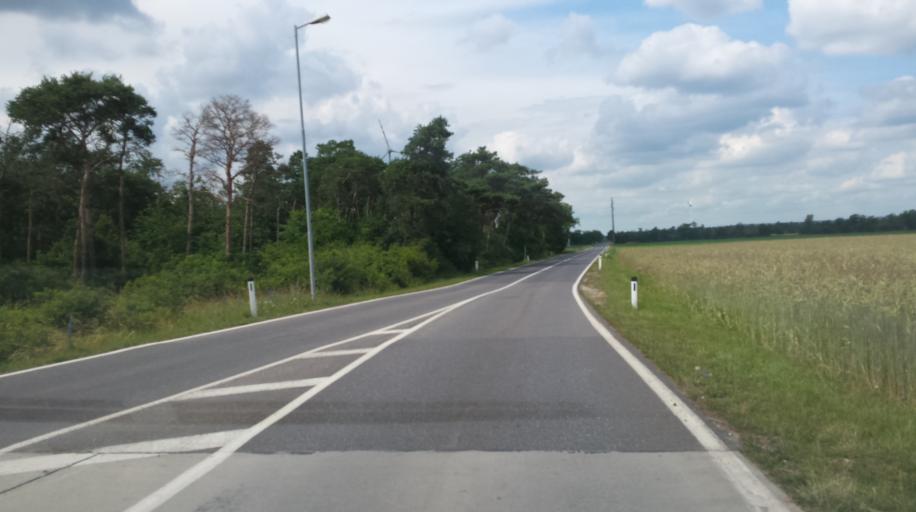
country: AT
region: Lower Austria
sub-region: Politischer Bezirk Mistelbach
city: Pillichsdorf
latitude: 48.3228
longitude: 16.5296
